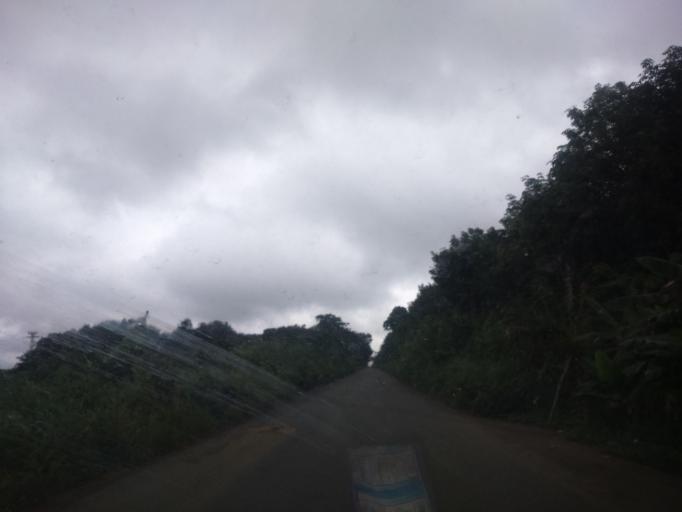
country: CI
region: Sud-Comoe
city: Bonoua
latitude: 5.2777
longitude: -3.5012
